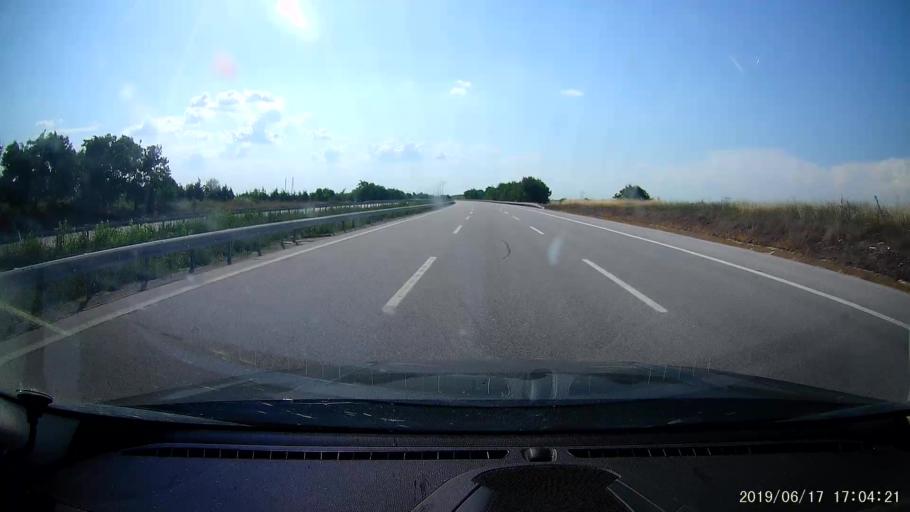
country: TR
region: Edirne
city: Haskoy
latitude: 41.6542
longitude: 26.7301
